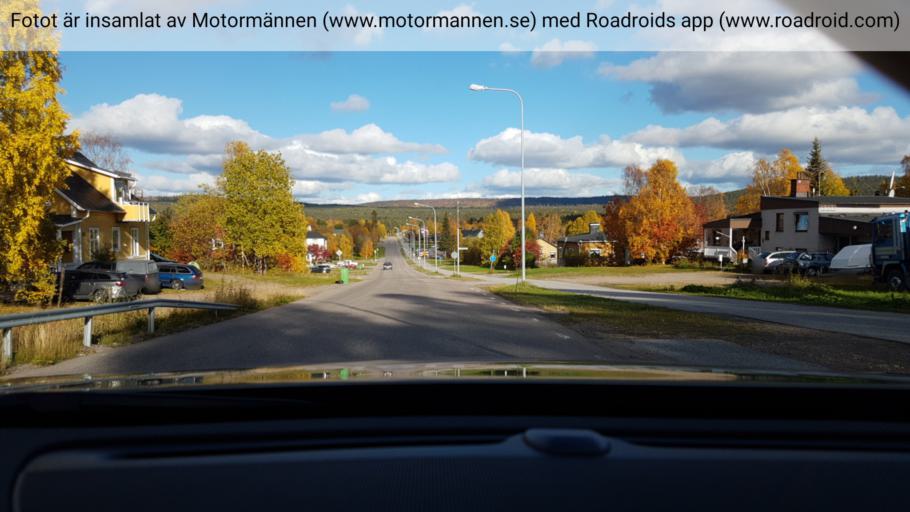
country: SE
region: Norrbotten
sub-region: Gallivare Kommun
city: Malmberget
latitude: 67.1856
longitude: 20.7399
